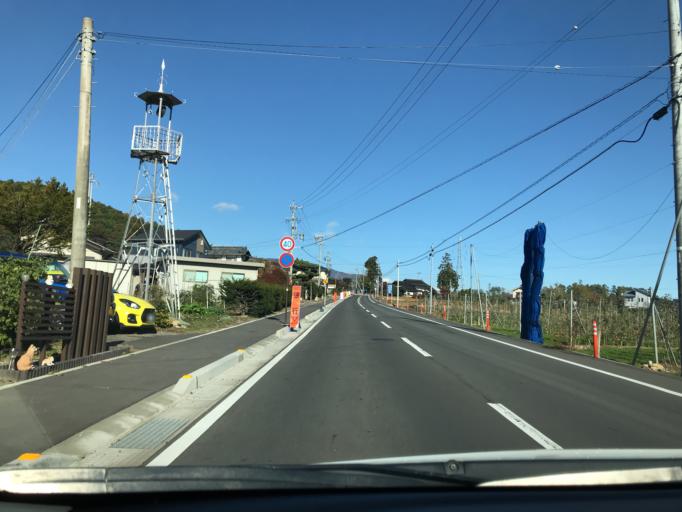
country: JP
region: Nagano
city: Matsumoto
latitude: 36.1760
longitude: 137.8675
